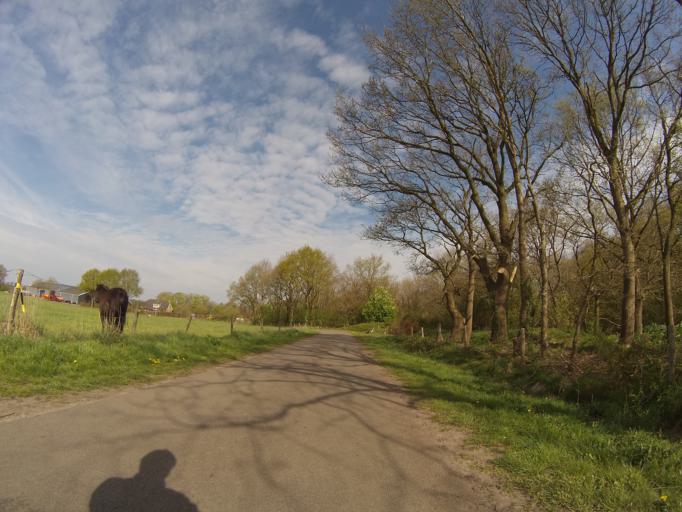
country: NL
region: Drenthe
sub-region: Gemeente Coevorden
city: Sleen
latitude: 52.7904
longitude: 6.7896
